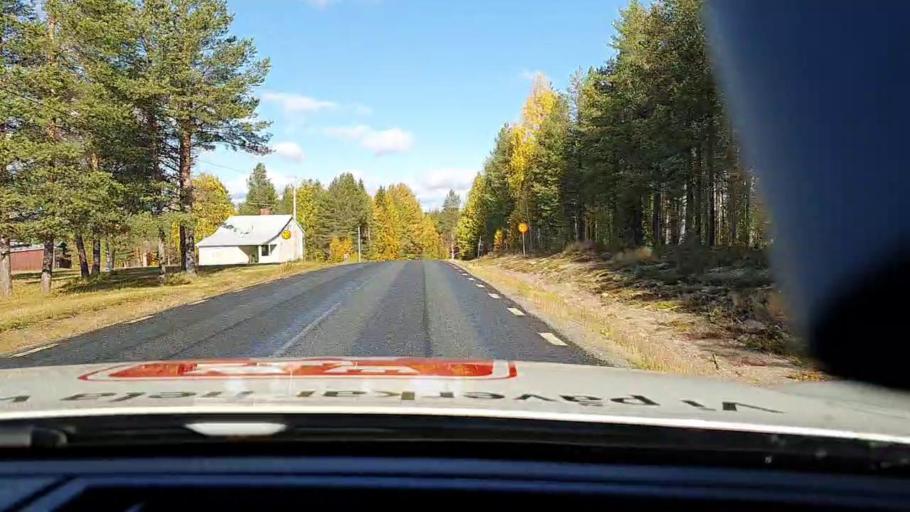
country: SE
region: Vaesterbotten
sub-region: Skelleftea Kommun
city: Langsele
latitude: 64.9989
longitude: 20.0904
